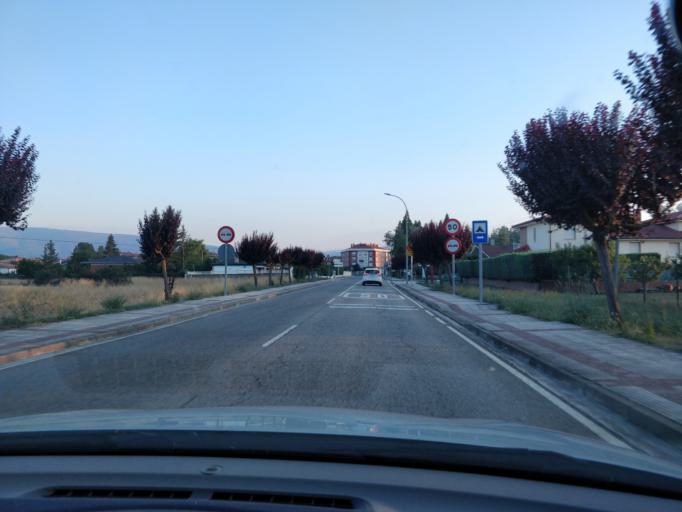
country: ES
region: Castille and Leon
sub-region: Provincia de Burgos
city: Medina de Pomar
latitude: 42.9459
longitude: -3.5639
